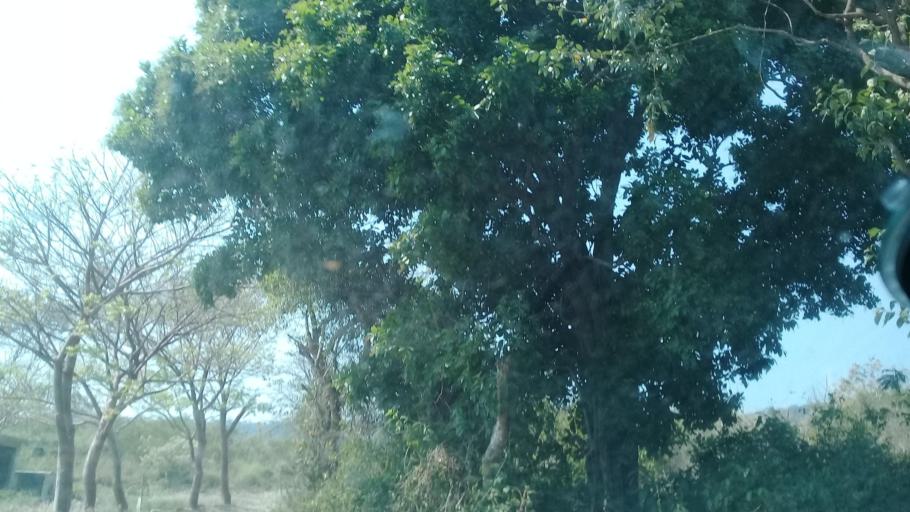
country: MX
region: Veracruz
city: El Castillo
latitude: 19.5668
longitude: -96.8346
